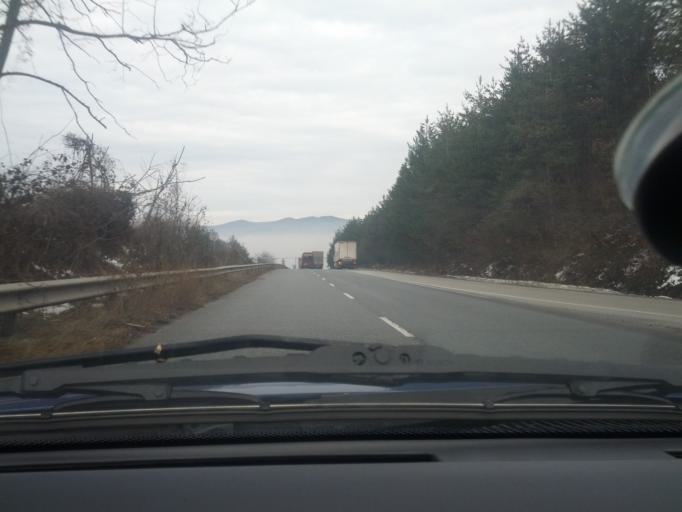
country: BG
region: Sofiya
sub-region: Obshtina Botevgrad
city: Botevgrad
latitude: 42.8929
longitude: 23.8263
